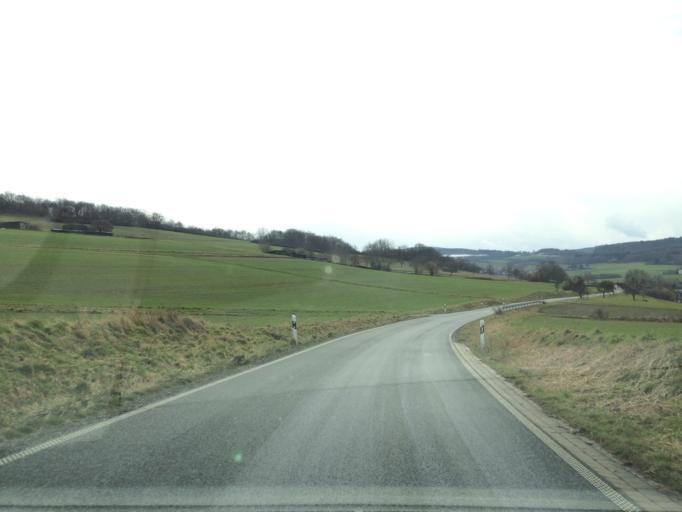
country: DE
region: Hesse
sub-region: Regierungsbezirk Darmstadt
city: Gravenwiesbach
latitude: 50.3520
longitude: 8.4352
